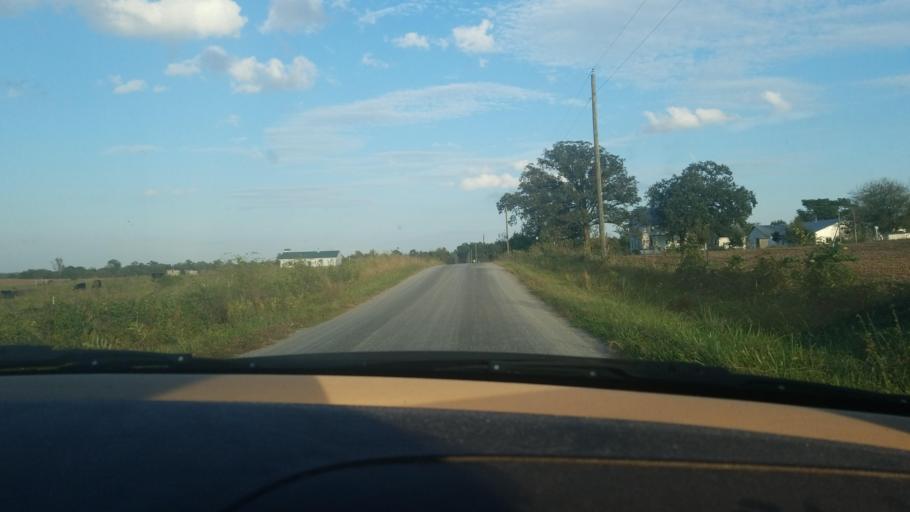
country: US
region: Illinois
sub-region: Saline County
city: Carrier Mills
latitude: 37.8050
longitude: -88.7051
